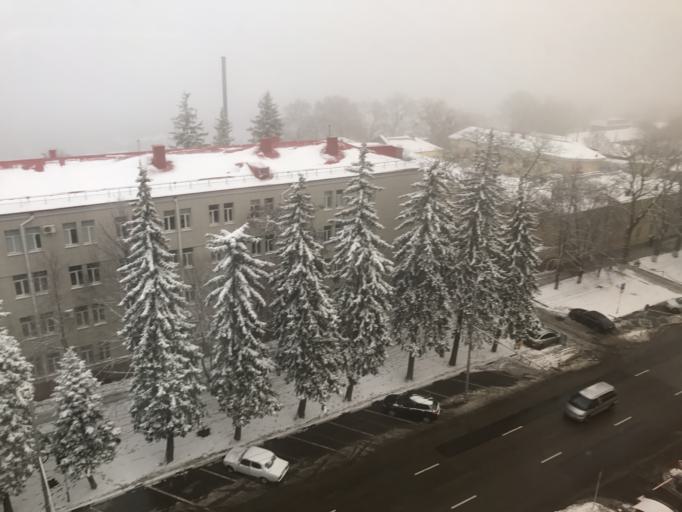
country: RU
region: Stavropol'skiy
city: Stavropol'
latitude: 45.0461
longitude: 41.9683
